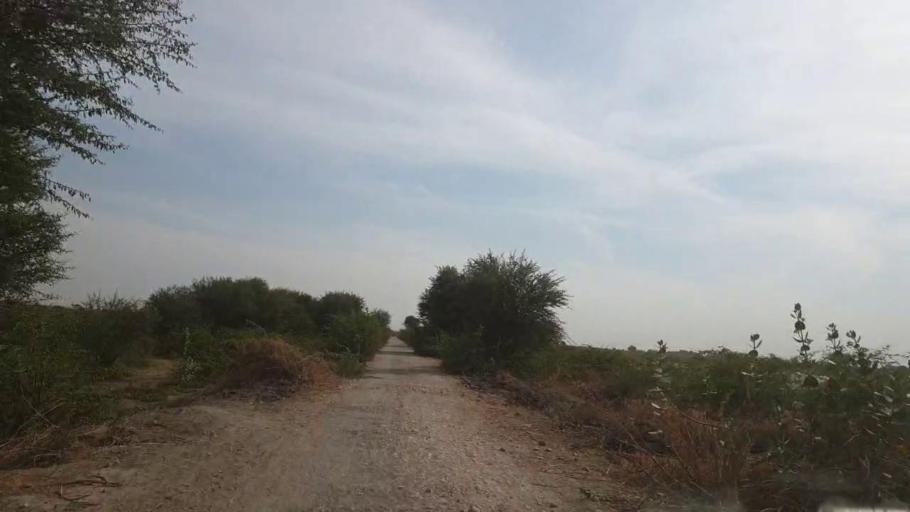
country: PK
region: Sindh
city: Nabisar
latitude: 25.0181
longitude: 69.5622
